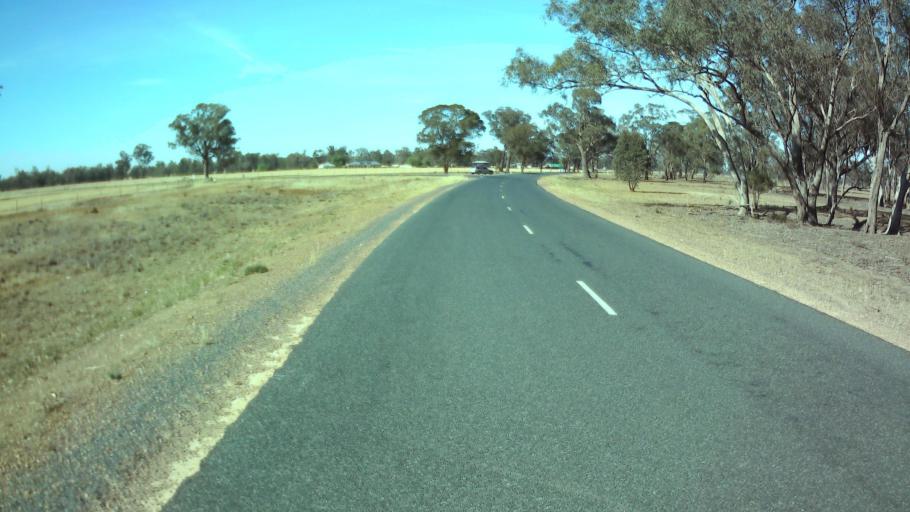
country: AU
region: New South Wales
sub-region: Weddin
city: Grenfell
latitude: -34.0959
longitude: 147.8855
